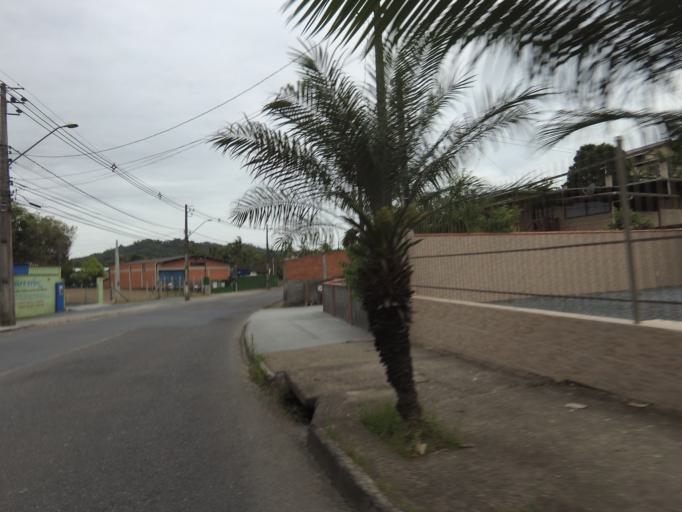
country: BR
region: Santa Catarina
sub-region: Blumenau
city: Blumenau
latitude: -26.8951
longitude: -49.1280
